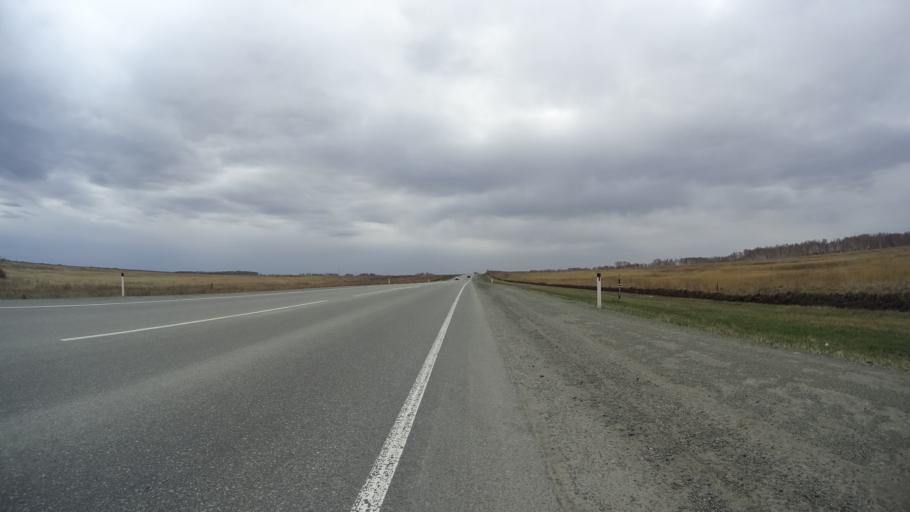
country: RU
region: Chelyabinsk
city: Yemanzhelinsk
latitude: 54.7104
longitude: 61.2597
